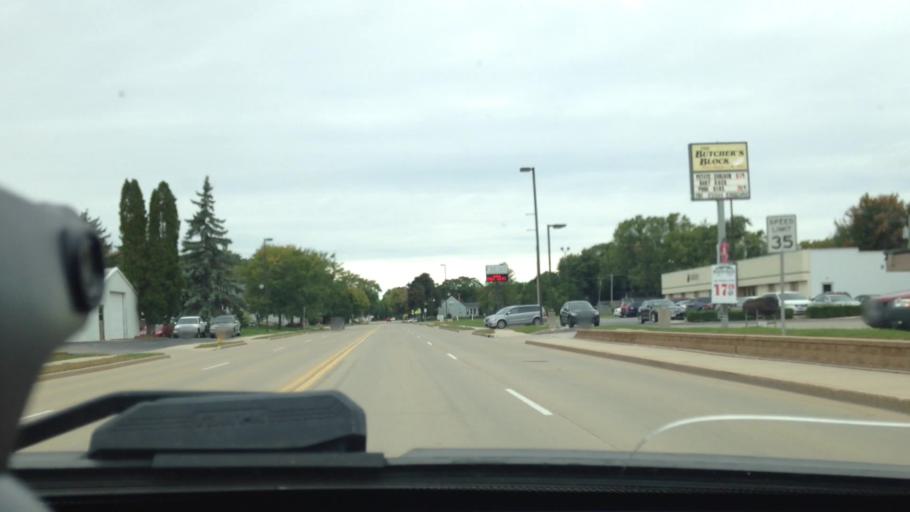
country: US
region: Wisconsin
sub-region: Fond du Lac County
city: North Fond du Lac
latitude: 43.8030
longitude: -88.4801
